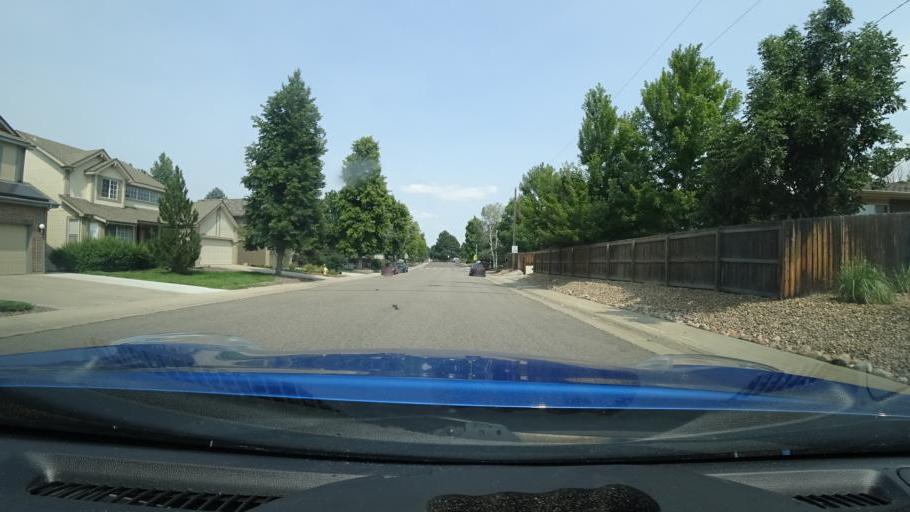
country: US
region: Colorado
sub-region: Adams County
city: Aurora
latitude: 39.6697
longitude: -104.8513
